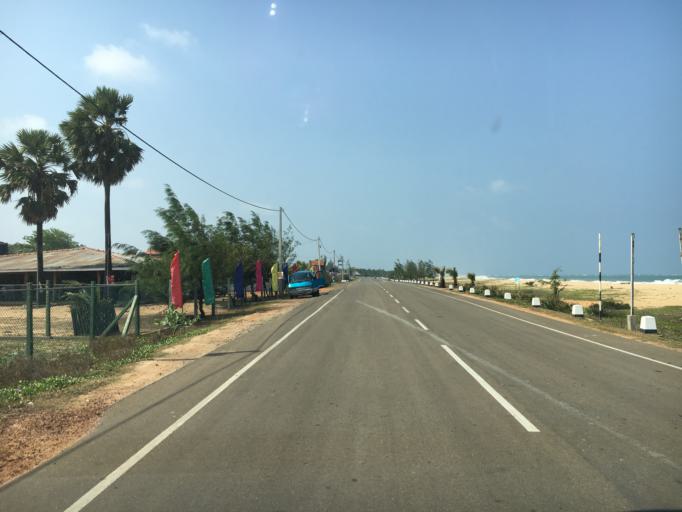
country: LK
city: Padaviya Divisional Secretariat
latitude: 9.2722
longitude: 80.8187
